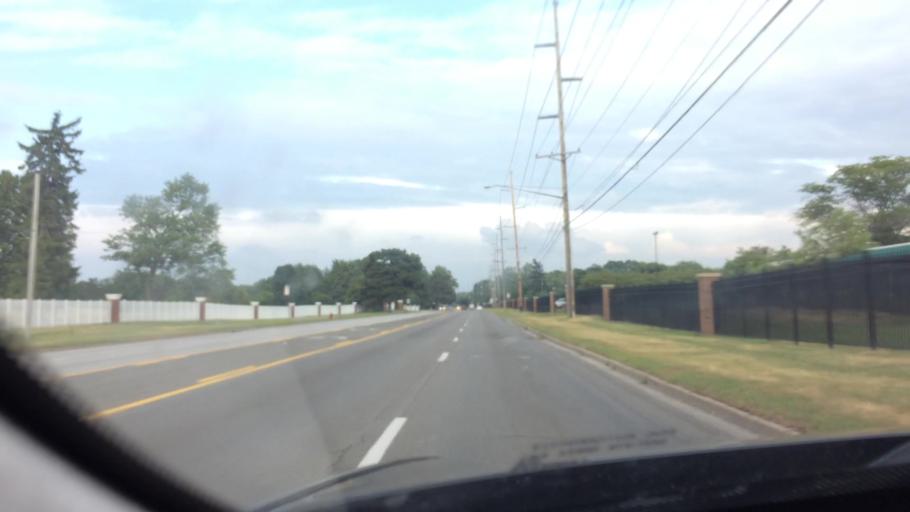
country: US
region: Ohio
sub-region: Lucas County
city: Ottawa Hills
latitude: 41.6529
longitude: -83.6512
